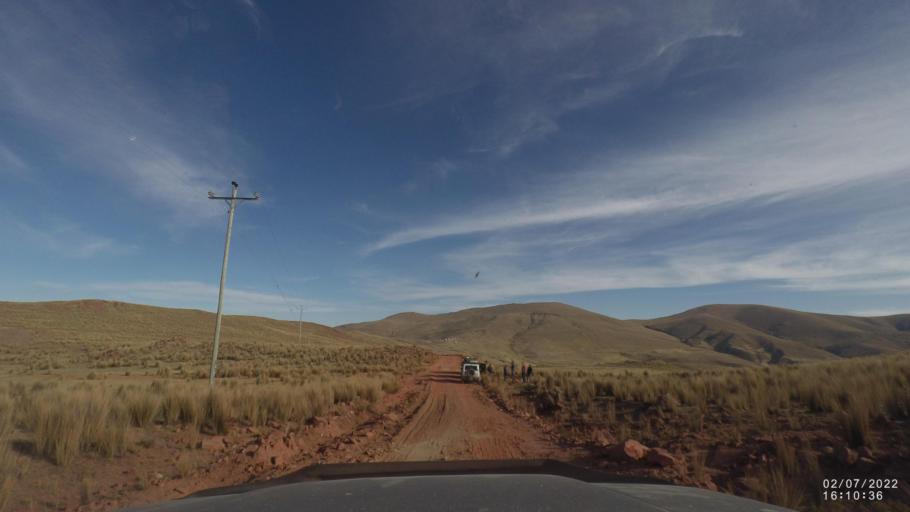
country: BO
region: Cochabamba
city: Irpa Irpa
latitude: -17.9134
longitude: -66.4400
